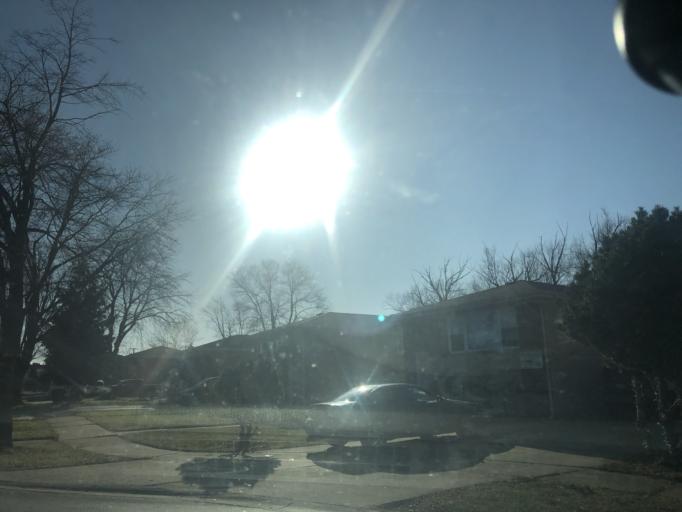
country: US
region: Illinois
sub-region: DuPage County
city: Addison
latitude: 41.9387
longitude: -87.9942
